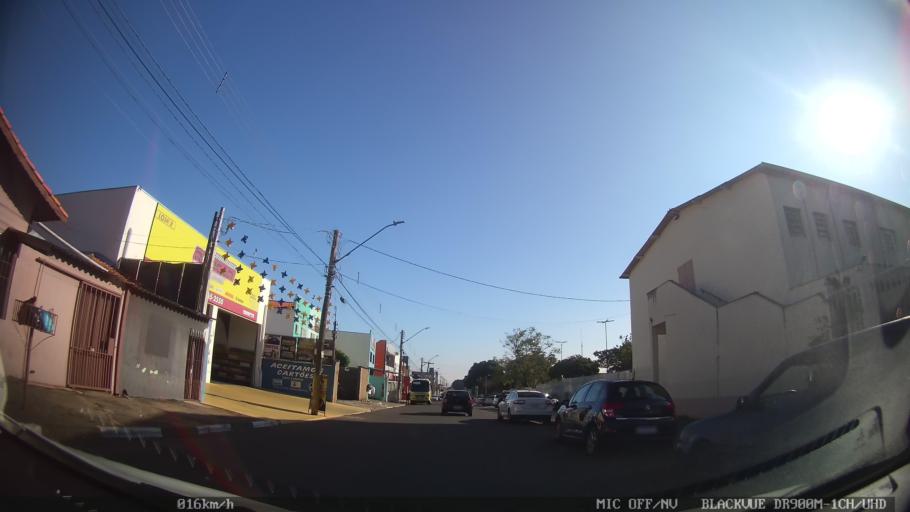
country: BR
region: Sao Paulo
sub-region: Hortolandia
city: Hortolandia
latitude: -22.8986
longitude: -47.1751
